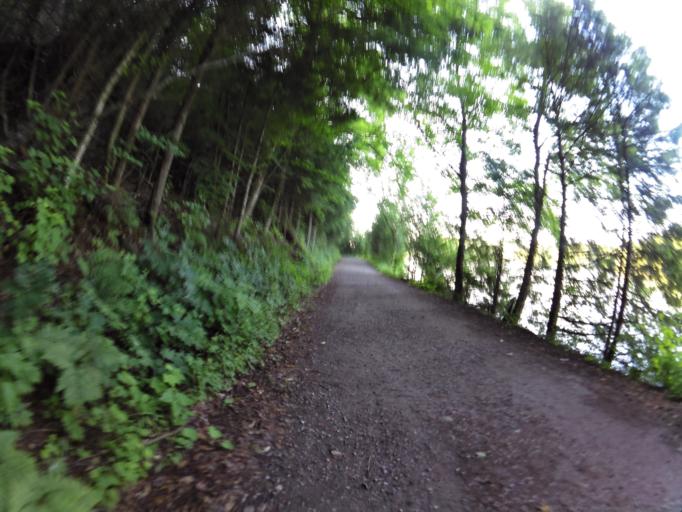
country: CA
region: Quebec
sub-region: Outaouais
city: Wakefield
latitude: 45.5906
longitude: -75.9845
